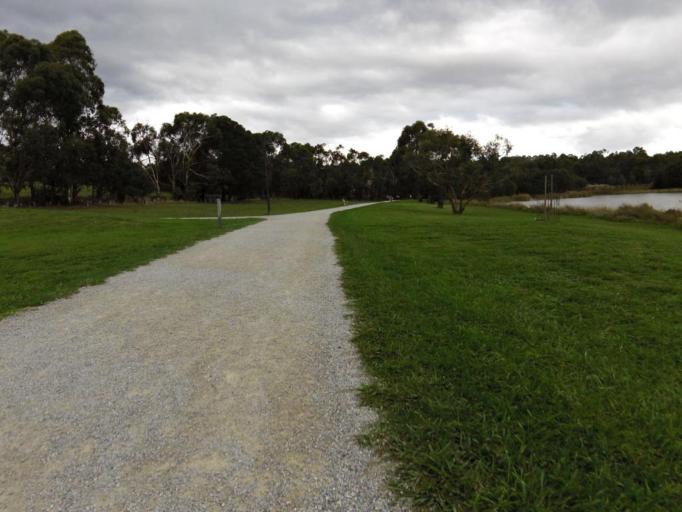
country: AU
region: Victoria
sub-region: Yarra Ranges
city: Lilydale
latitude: -37.7684
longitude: 145.3544
